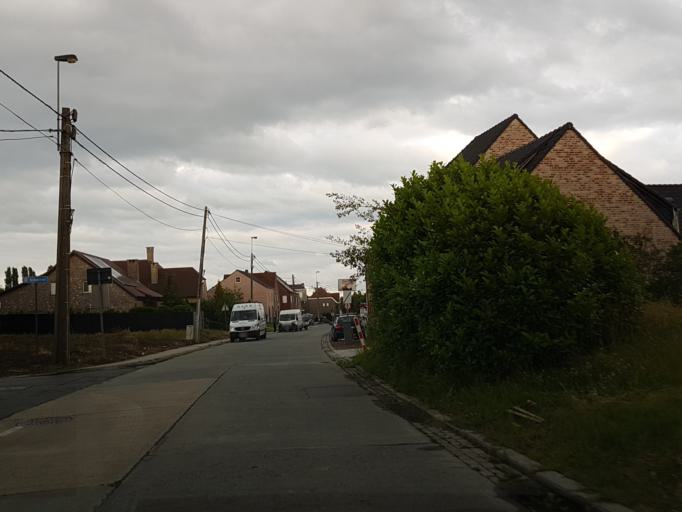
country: BE
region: Flanders
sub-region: Provincie Vlaams-Brabant
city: Opwijk
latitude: 50.9936
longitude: 4.1800
